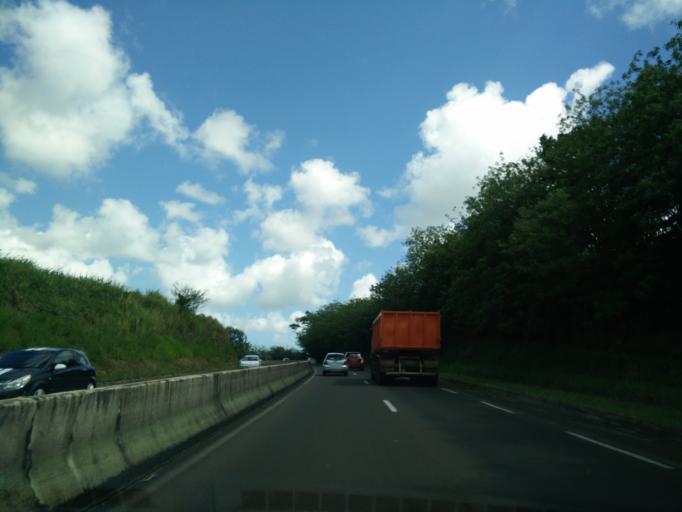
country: MQ
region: Martinique
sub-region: Martinique
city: Ducos
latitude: 14.5641
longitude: -60.9789
